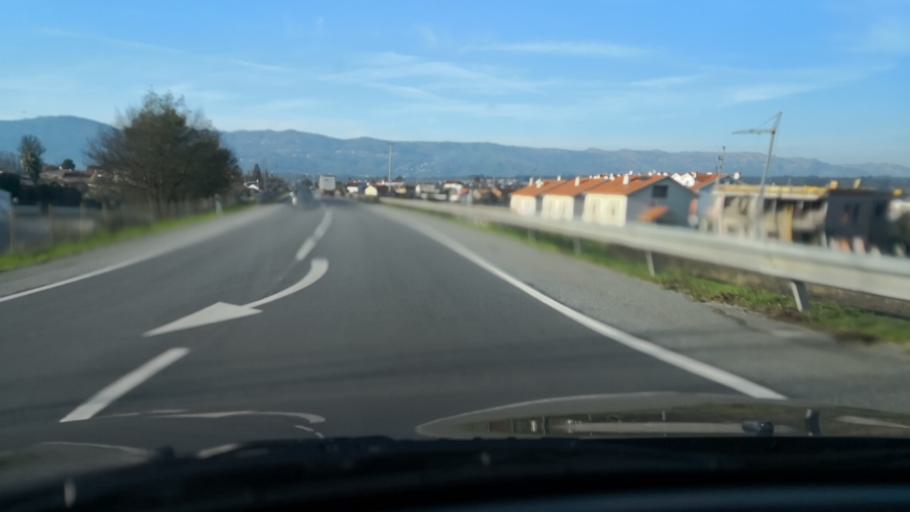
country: PT
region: Viseu
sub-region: Concelho de Tondela
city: Tondela
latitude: 40.5108
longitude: -8.0870
